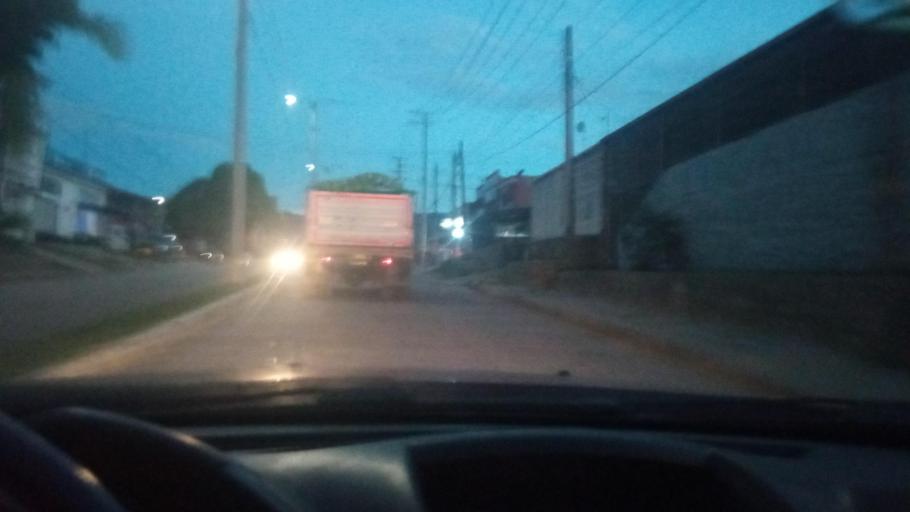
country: CO
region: Huila
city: Pitalito
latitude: 1.8581
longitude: -76.0475
